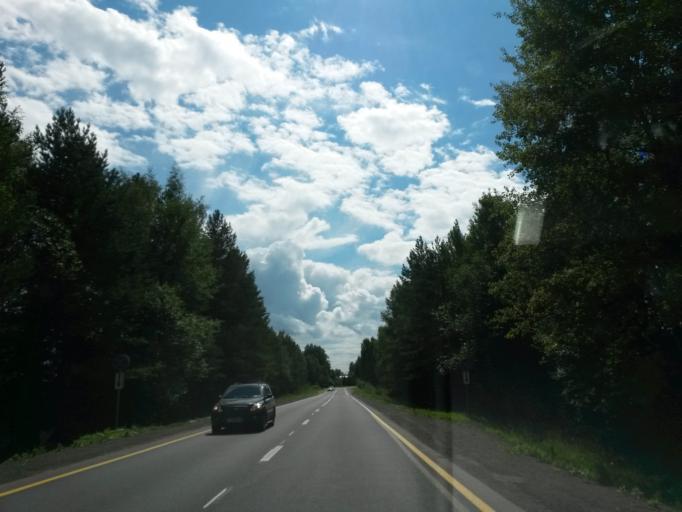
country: RU
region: Jaroslavl
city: Gavrilov-Yam
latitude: 57.2853
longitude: 39.9532
